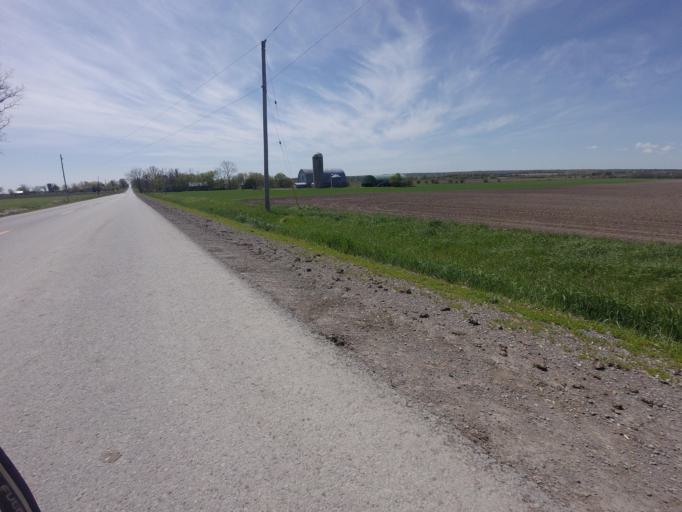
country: CA
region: Ontario
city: Arnprior
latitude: 45.3947
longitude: -76.1455
